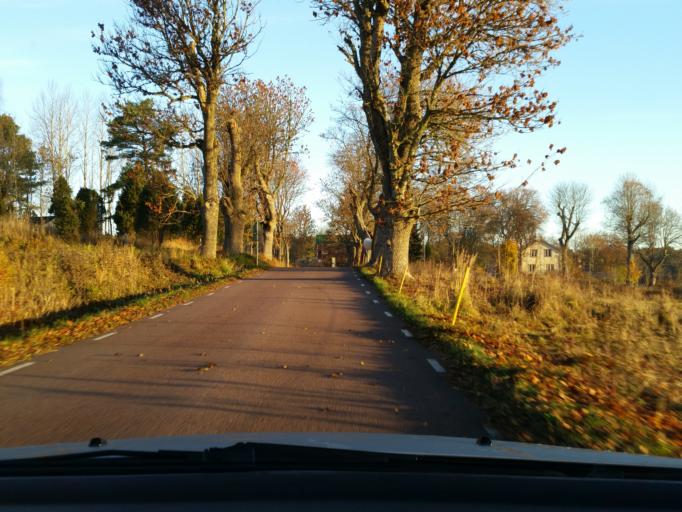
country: AX
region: Alands landsbygd
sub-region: Sund
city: Sund
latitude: 60.2342
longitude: 20.0753
